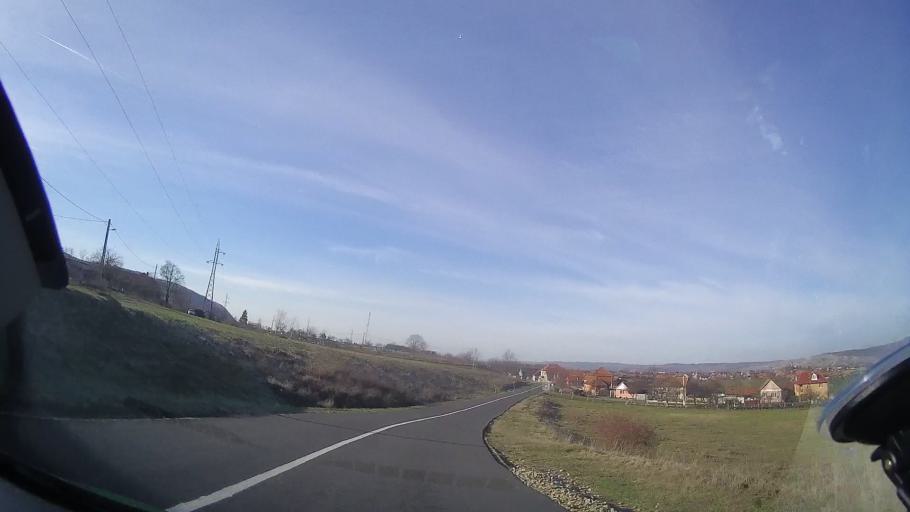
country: RO
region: Bihor
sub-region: Comuna Astileu
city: Astileu
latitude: 47.0262
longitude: 22.4019
